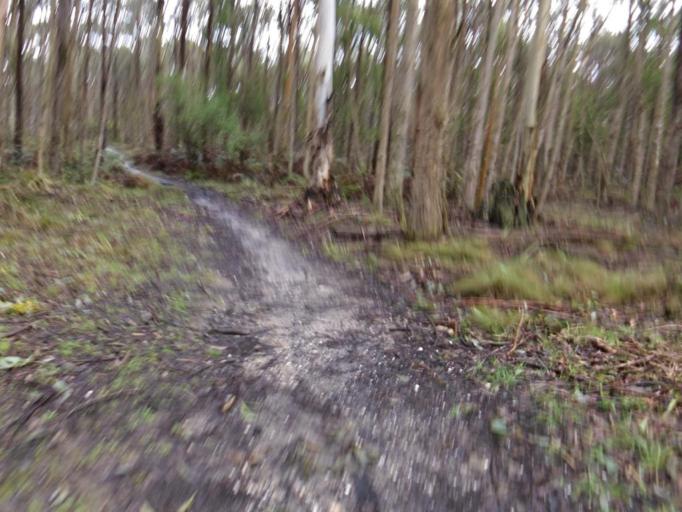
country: AU
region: Victoria
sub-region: Moorabool
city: Bacchus Marsh
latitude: -37.4057
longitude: 144.4899
